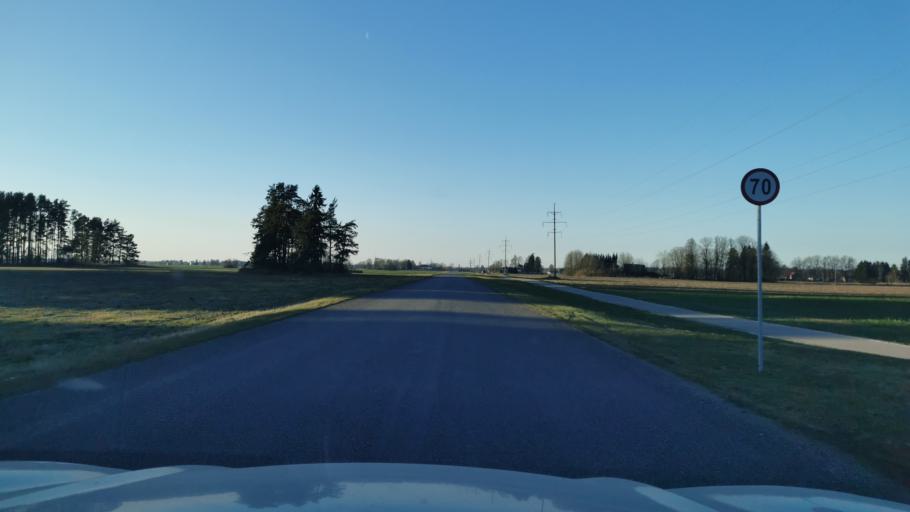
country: EE
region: Ida-Virumaa
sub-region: Puessi linn
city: Pussi
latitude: 59.3431
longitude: 27.0405
